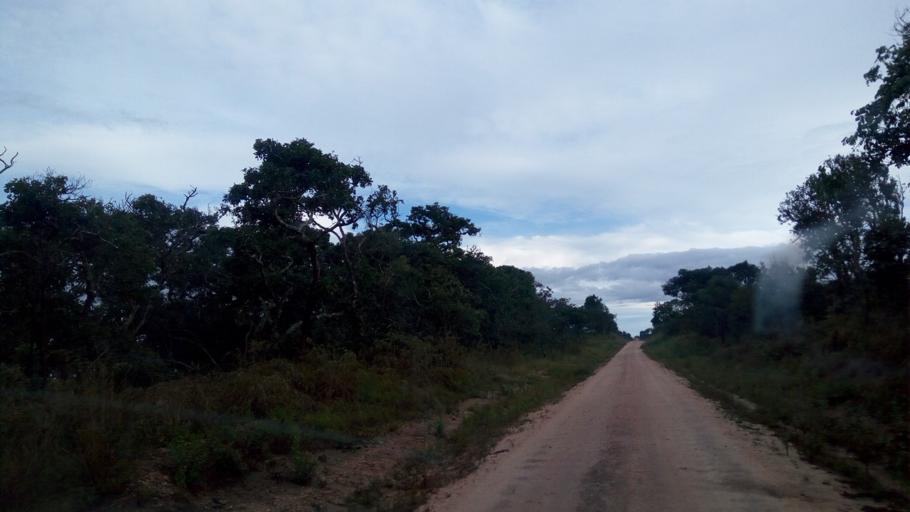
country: CD
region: Katanga
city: Kalemie
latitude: -6.5934
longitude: 29.0400
